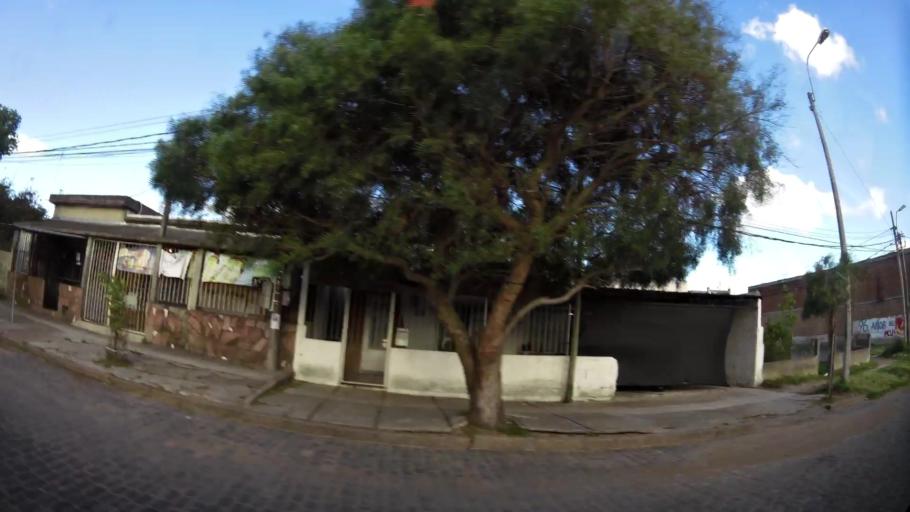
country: UY
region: Montevideo
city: Montevideo
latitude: -34.8816
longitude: -56.2648
